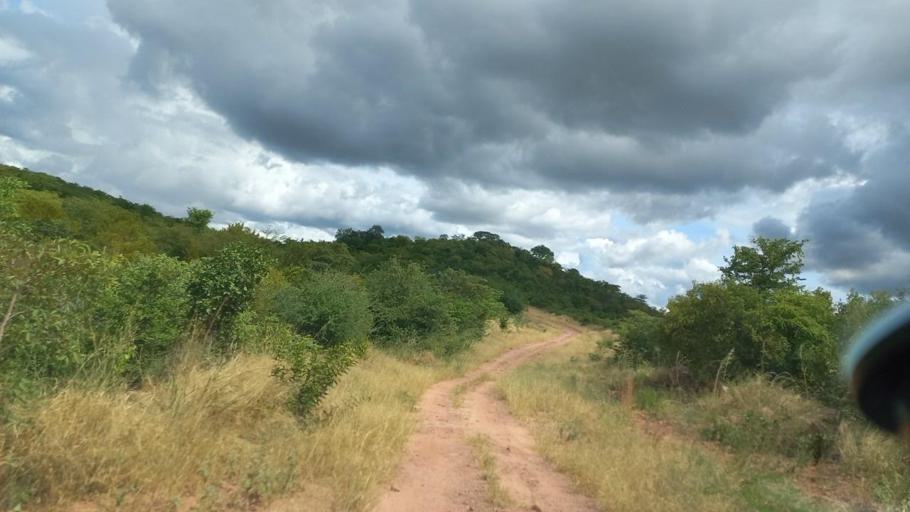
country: ZM
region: Lusaka
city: Luangwa
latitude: -15.6335
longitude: 30.3848
